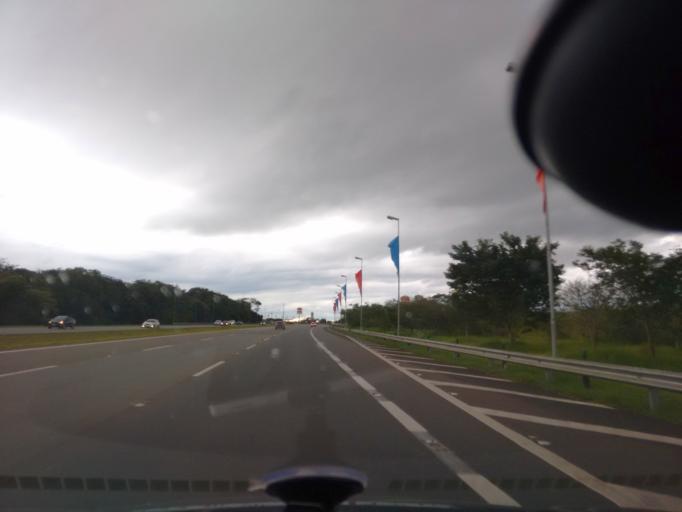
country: BR
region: Sao Paulo
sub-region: Santa Barbara D'Oeste
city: Santa Barbara d'Oeste
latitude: -22.8230
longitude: -47.3757
